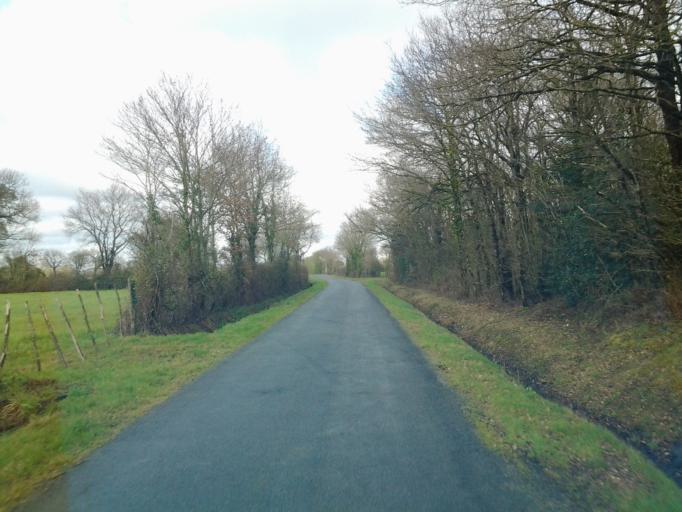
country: FR
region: Pays de la Loire
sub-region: Departement de la Vendee
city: Nesmy
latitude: 46.6500
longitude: -1.3612
